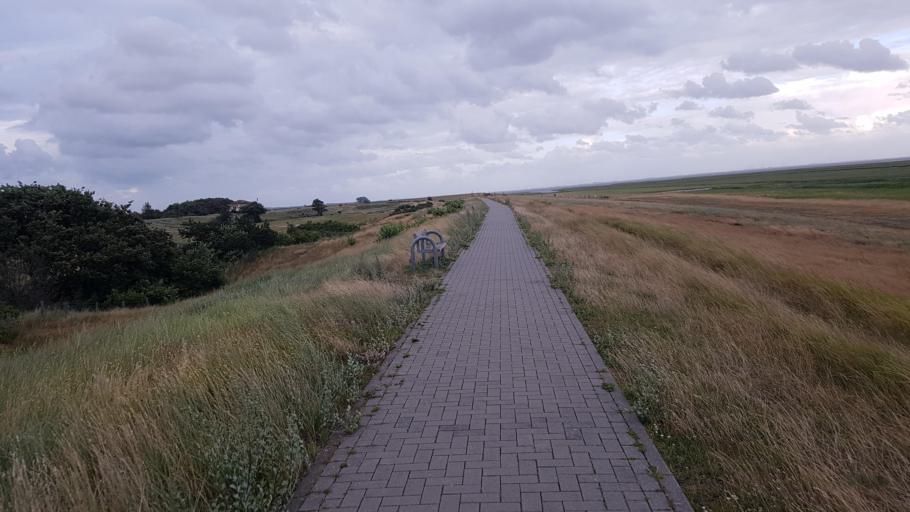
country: DE
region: Schleswig-Holstein
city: Sankt Peter-Ording
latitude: 54.2800
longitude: 8.6707
